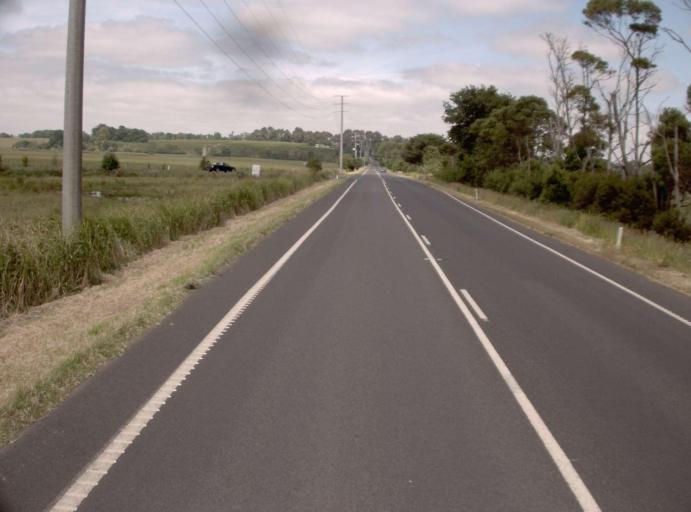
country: AU
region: Victoria
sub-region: Baw Baw
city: Warragul
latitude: -38.4571
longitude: 145.9729
